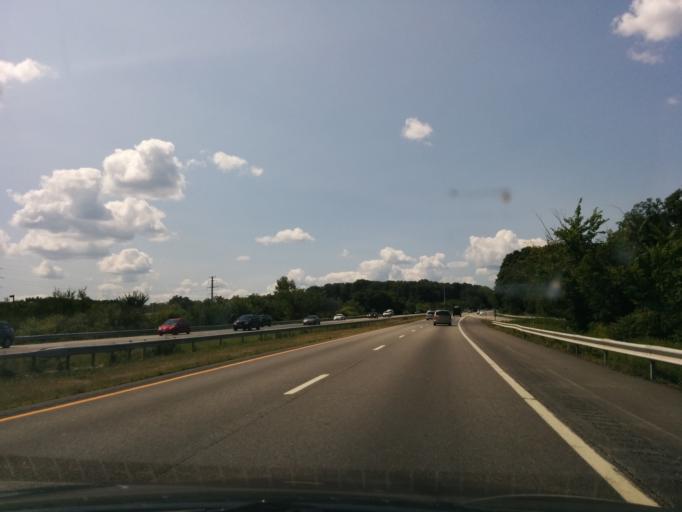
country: US
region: New York
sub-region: Orange County
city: Harriman
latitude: 41.3197
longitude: -74.1461
